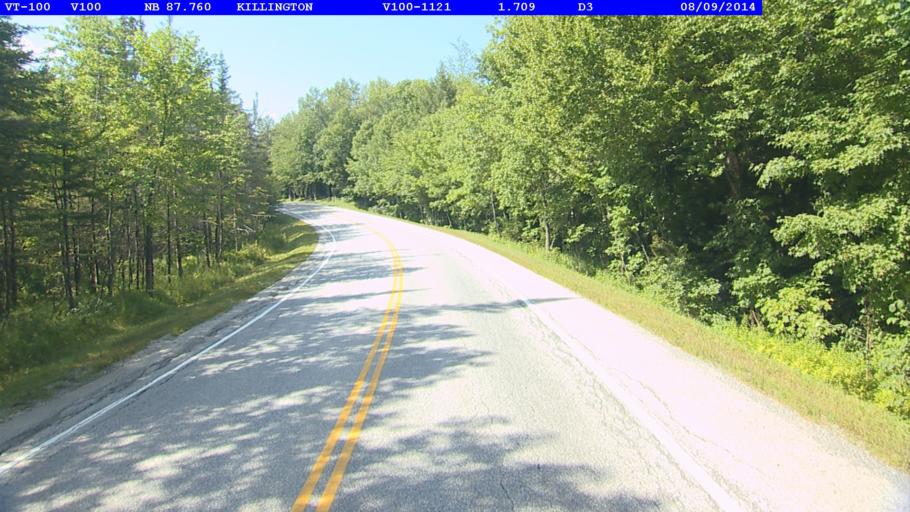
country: US
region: Vermont
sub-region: Rutland County
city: Rutland
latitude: 43.6903
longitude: -72.8119
